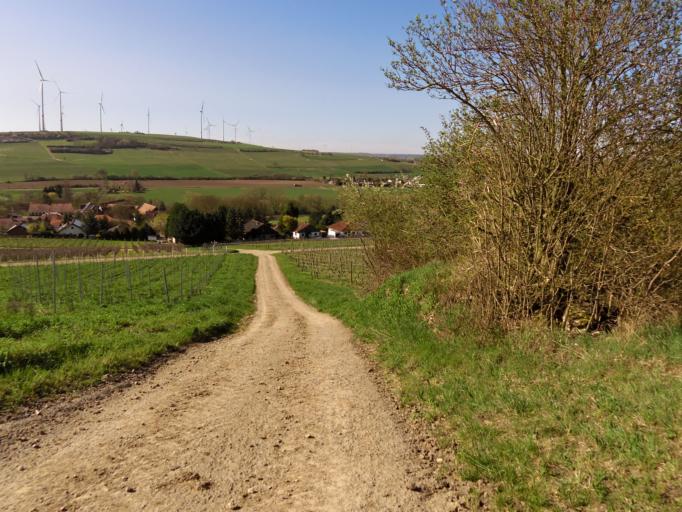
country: DE
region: Rheinland-Pfalz
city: Molsheim
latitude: 49.6469
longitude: 8.1488
